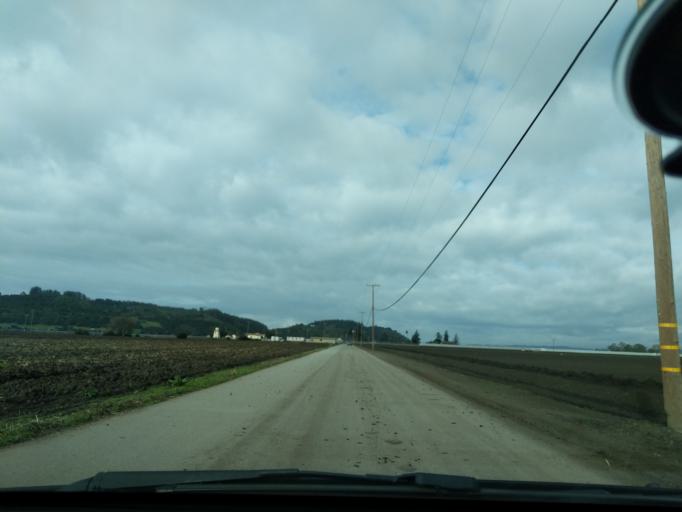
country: US
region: California
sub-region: San Benito County
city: Aromas
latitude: 36.8971
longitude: -121.6706
